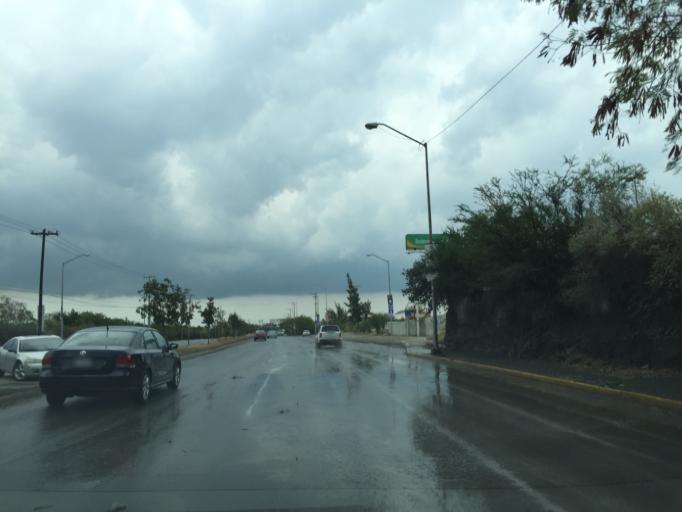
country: MX
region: Nuevo Leon
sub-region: Juarez
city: Valle de Juarez
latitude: 25.6757
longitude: -100.1679
